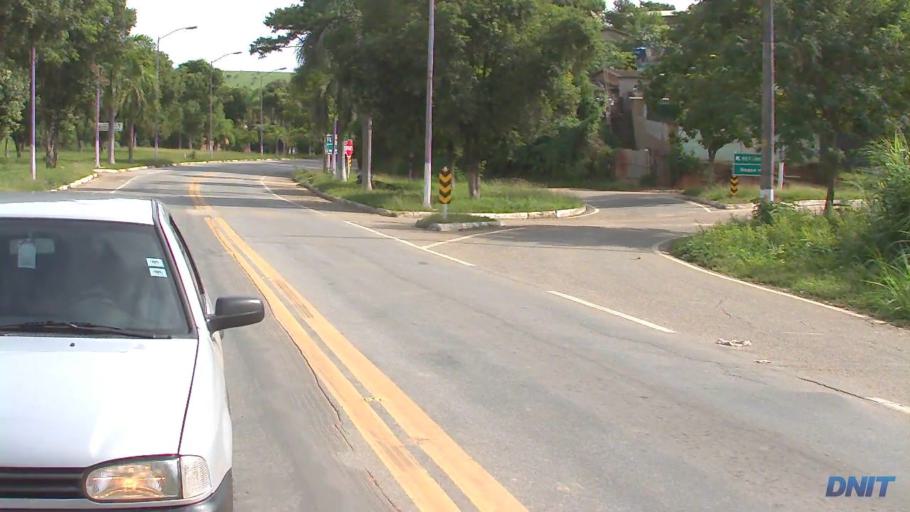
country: BR
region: Minas Gerais
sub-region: Belo Oriente
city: Belo Oriente
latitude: -19.2326
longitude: -42.3286
